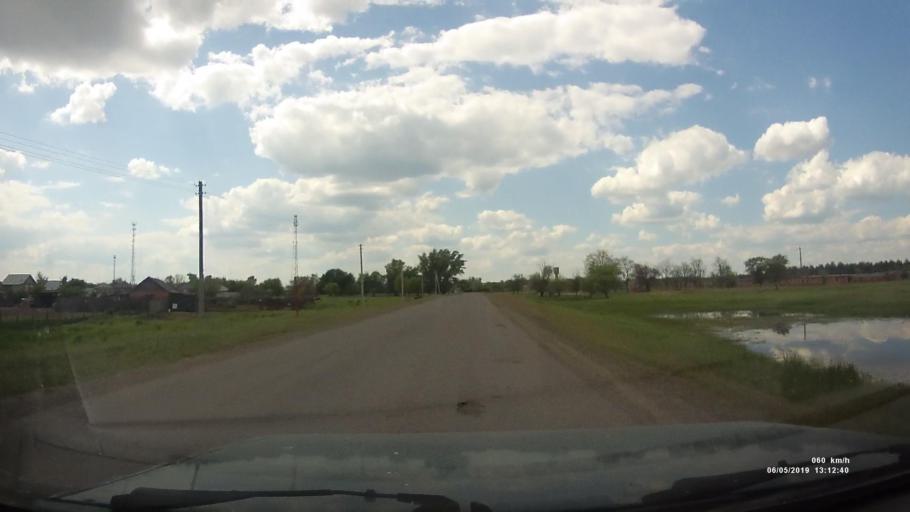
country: RU
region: Rostov
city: Ust'-Donetskiy
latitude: 47.7553
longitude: 40.9441
